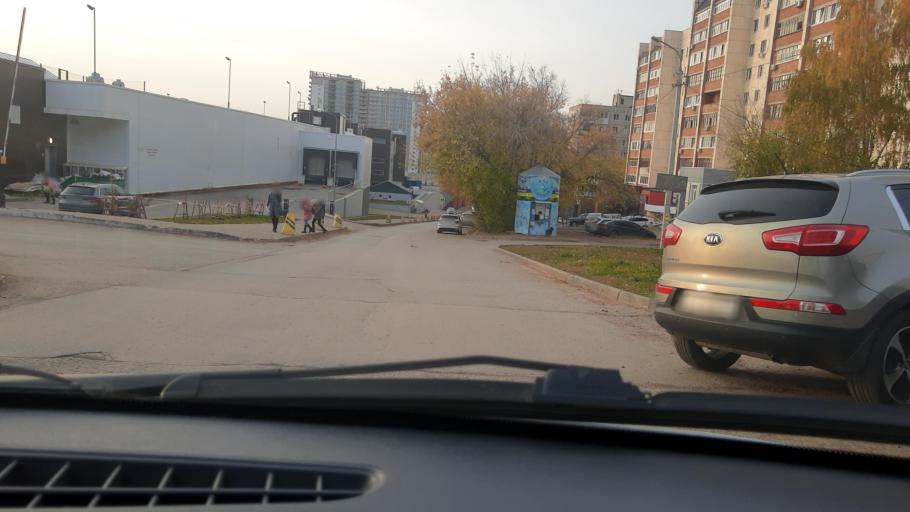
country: RU
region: Bashkortostan
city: Ufa
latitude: 54.7198
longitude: 56.0040
